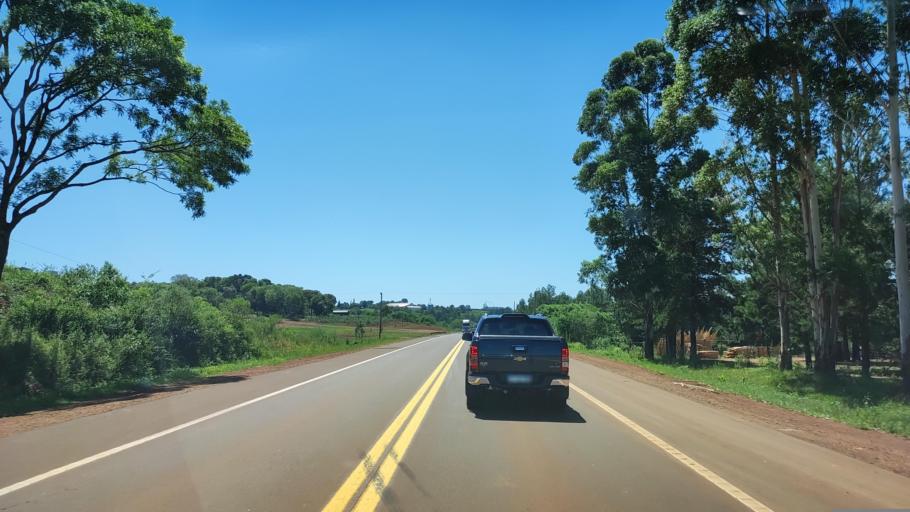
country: AR
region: Misiones
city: Aristobulo del Valle
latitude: -27.0867
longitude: -54.7918
